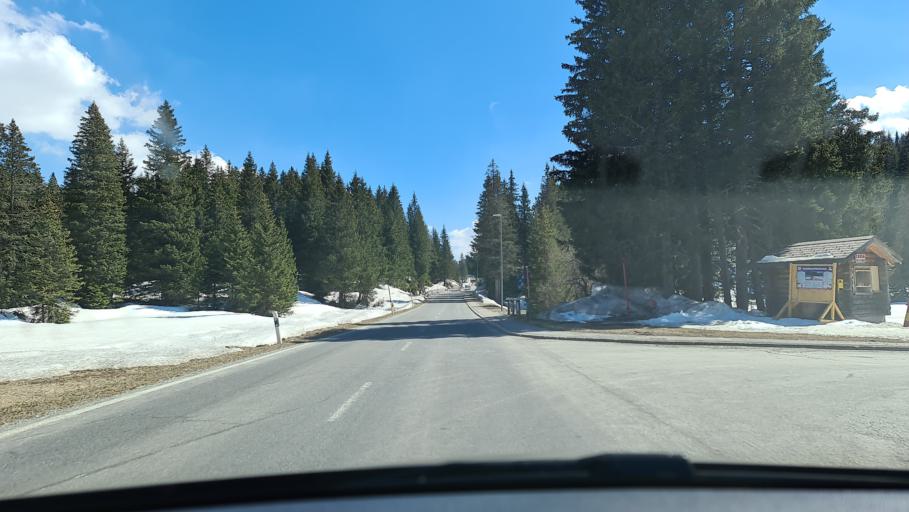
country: CH
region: Grisons
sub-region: Moesa District
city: Mesocco
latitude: 46.4541
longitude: 9.1984
